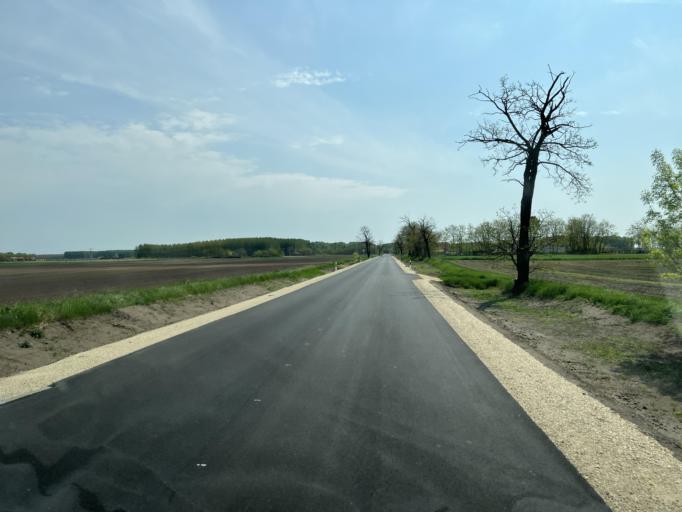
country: HU
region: Pest
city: Nagykoros
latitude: 47.0218
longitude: 19.8383
